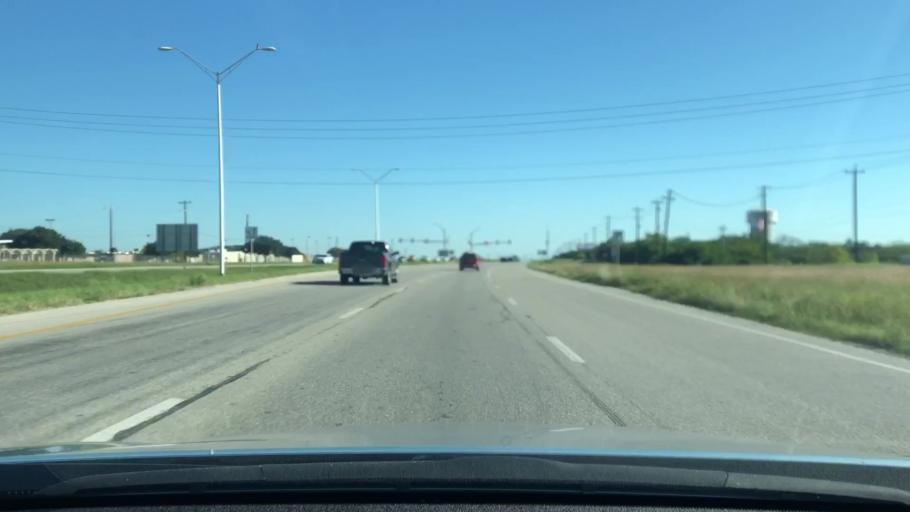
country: US
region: Texas
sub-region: Bexar County
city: Universal City
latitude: 29.5294
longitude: -98.2989
